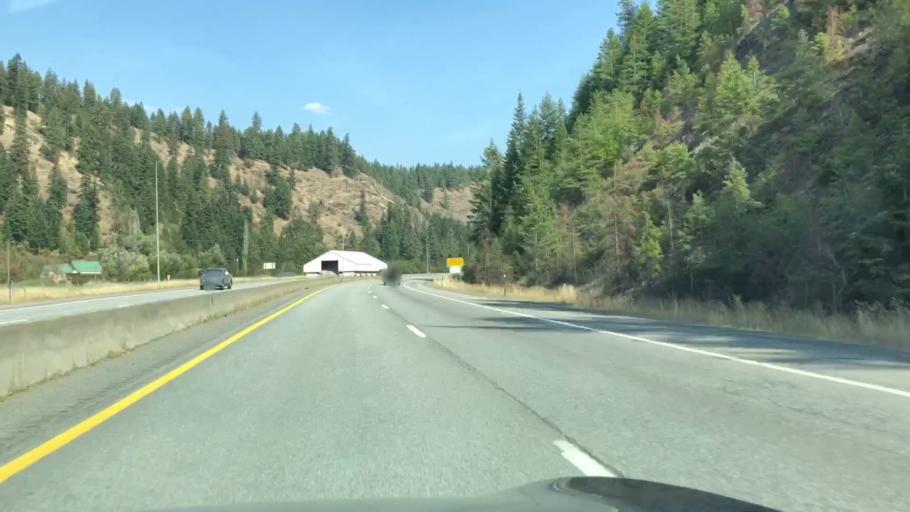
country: US
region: Idaho
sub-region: Kootenai County
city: Coeur d'Alene
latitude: 47.6303
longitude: -116.6134
